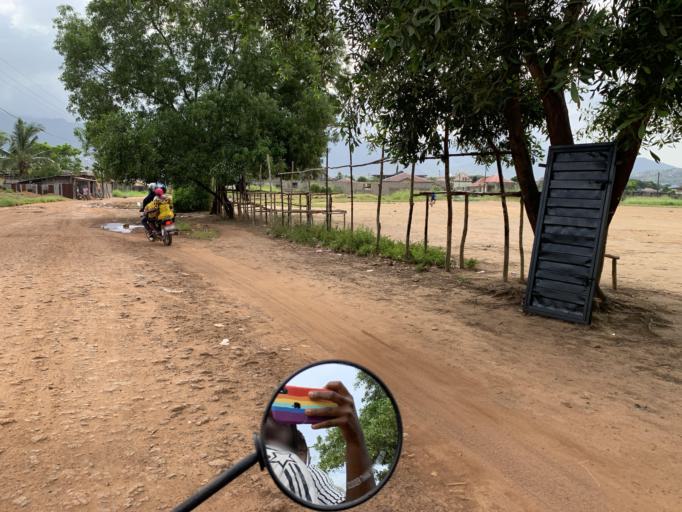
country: SL
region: Western Area
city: Hastings
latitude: 8.3960
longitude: -13.1181
